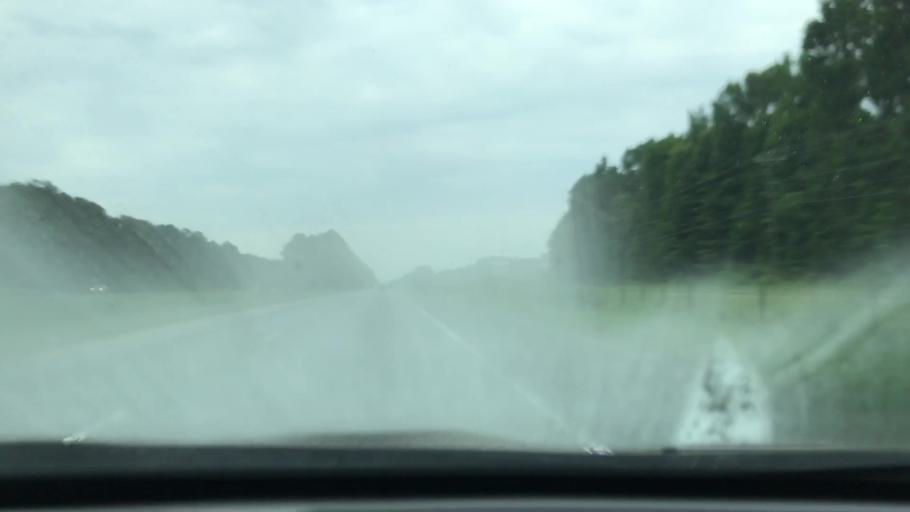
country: US
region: South Carolina
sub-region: Jasper County
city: Ridgeland
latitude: 32.5298
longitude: -80.9590
